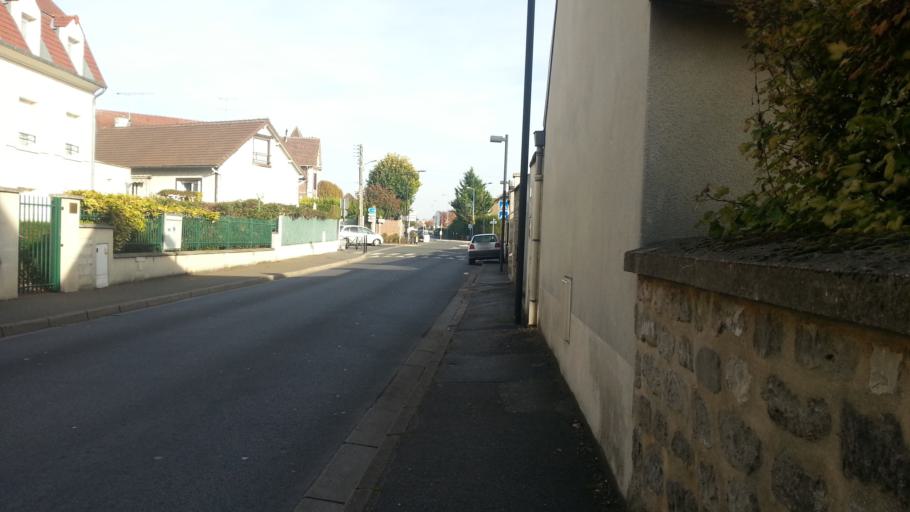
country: FR
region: Picardie
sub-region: Departement de l'Oise
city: Chambly
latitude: 49.1668
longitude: 2.2472
